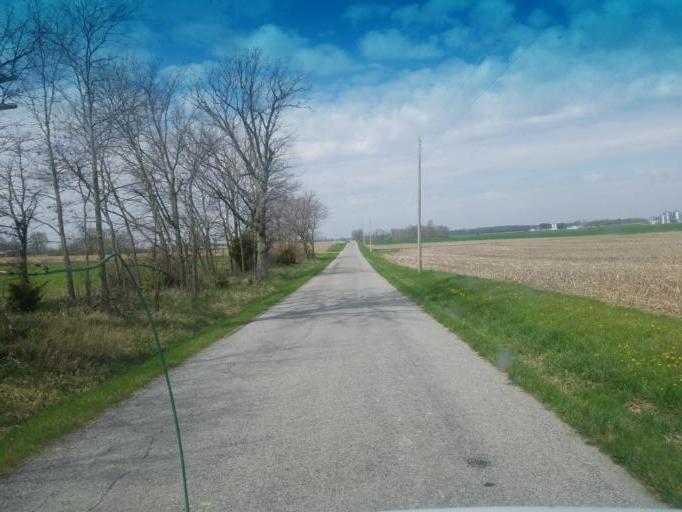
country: US
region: Ohio
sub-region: Logan County
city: Northwood
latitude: 40.4897
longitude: -83.7480
